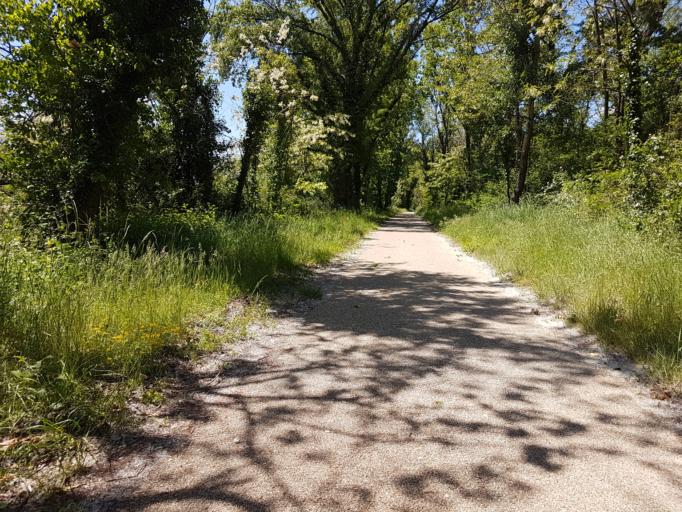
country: FR
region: Rhone-Alpes
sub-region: Departement de la Drome
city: Saint-Vallier
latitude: 45.1409
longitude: 4.8121
